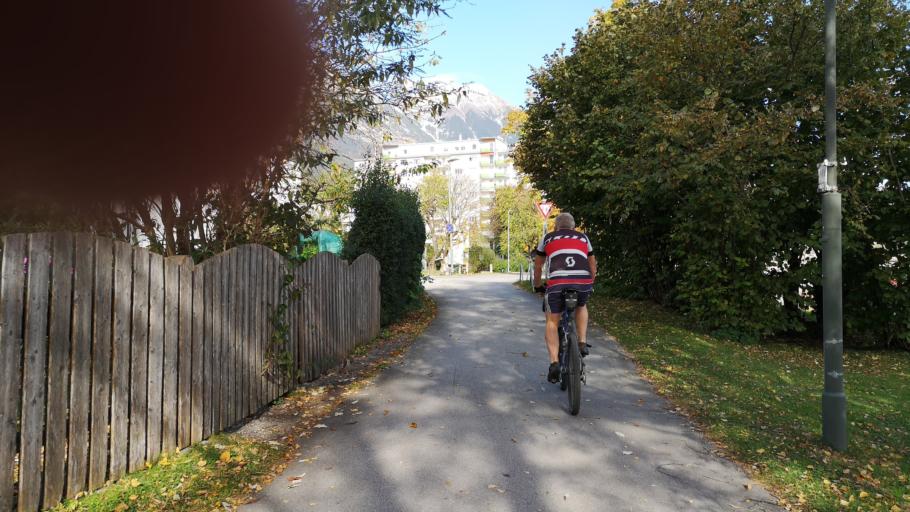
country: AT
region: Tyrol
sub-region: Innsbruck Stadt
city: Innsbruck
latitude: 47.2637
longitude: 11.3820
